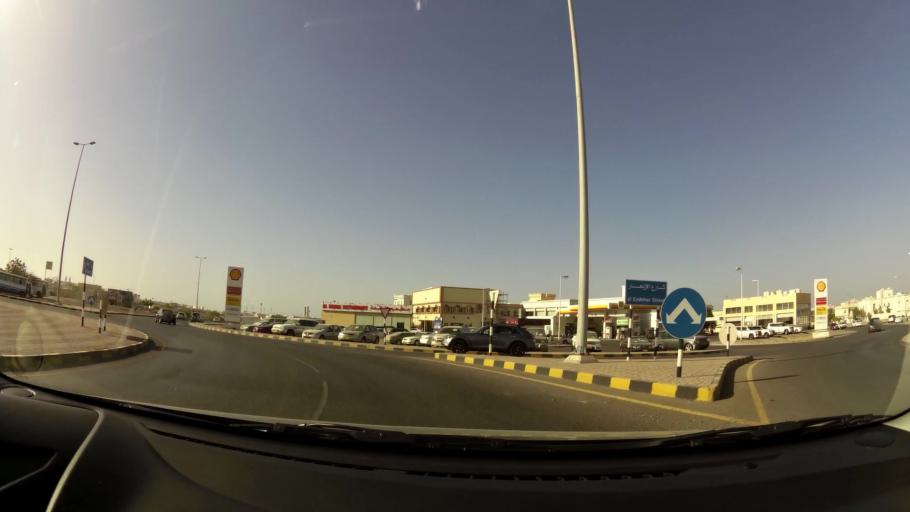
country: OM
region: Muhafazat Masqat
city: As Sib al Jadidah
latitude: 23.6016
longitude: 58.2174
